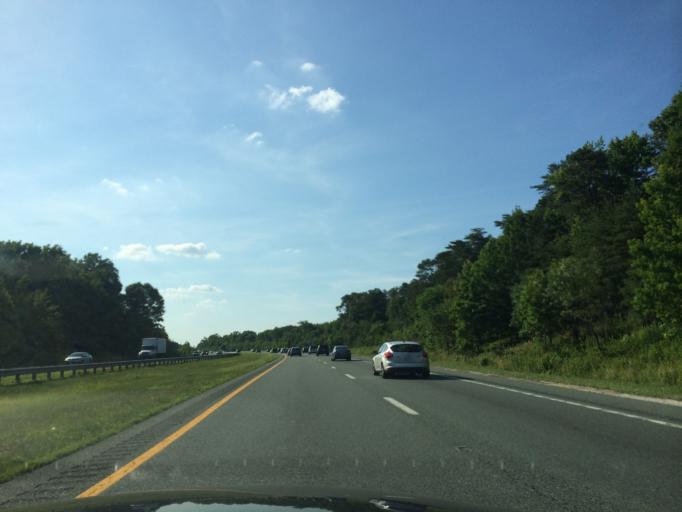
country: US
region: Maryland
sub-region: Anne Arundel County
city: Severn
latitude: 39.1517
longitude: -76.7085
